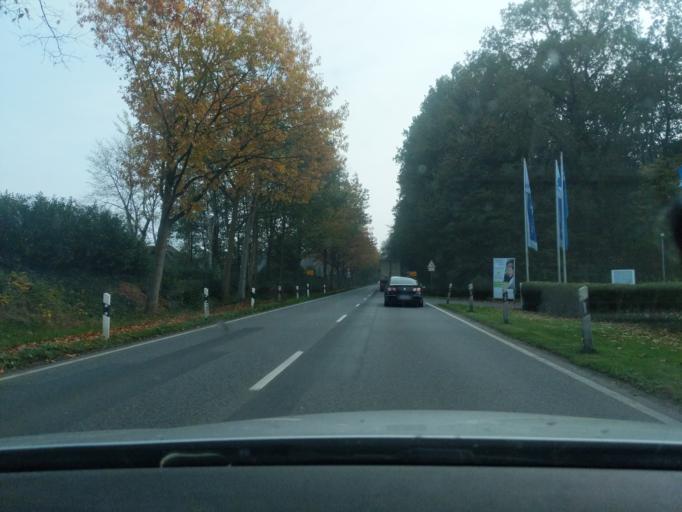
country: DE
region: Lower Saxony
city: Himmelpforten
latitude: 53.6102
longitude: 9.3142
